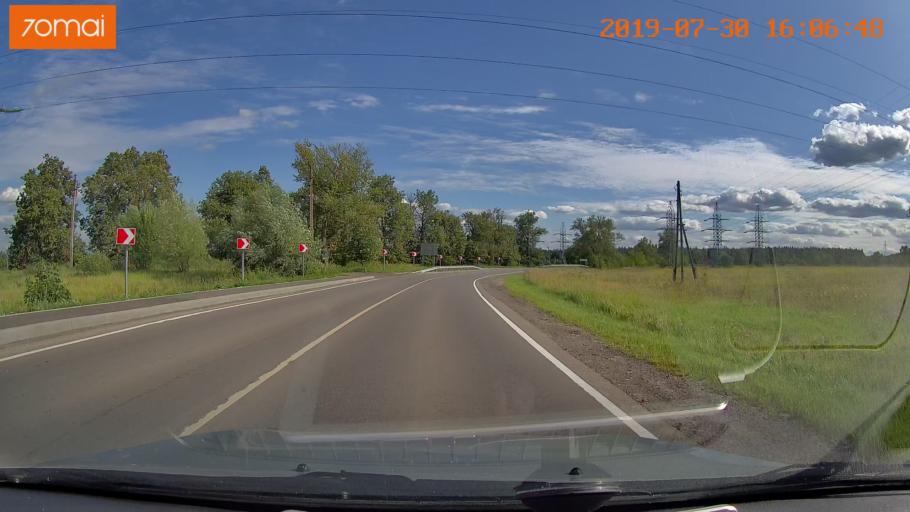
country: RU
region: Moskovskaya
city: Peski
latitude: 55.2525
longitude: 38.7194
